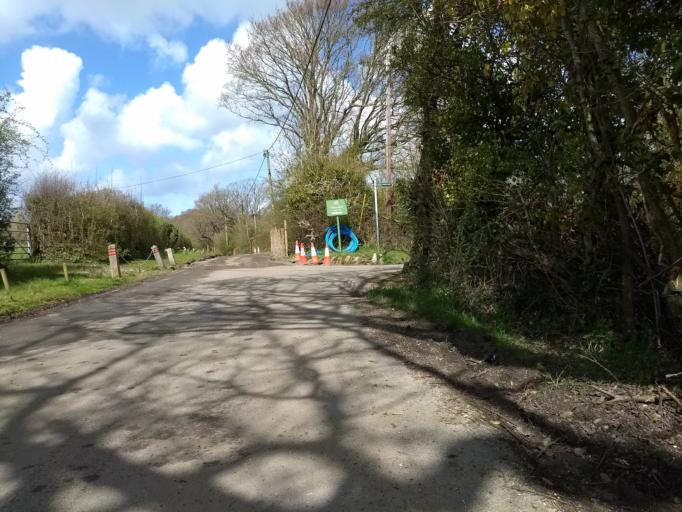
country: GB
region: England
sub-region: Isle of Wight
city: East Cowes
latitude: 50.7392
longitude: -1.2291
